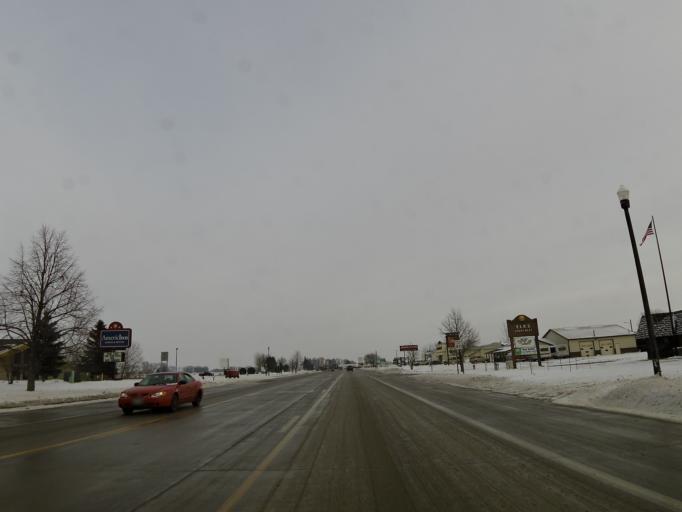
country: US
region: Minnesota
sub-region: McLeod County
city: Hutchinson
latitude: 44.8954
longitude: -94.3490
